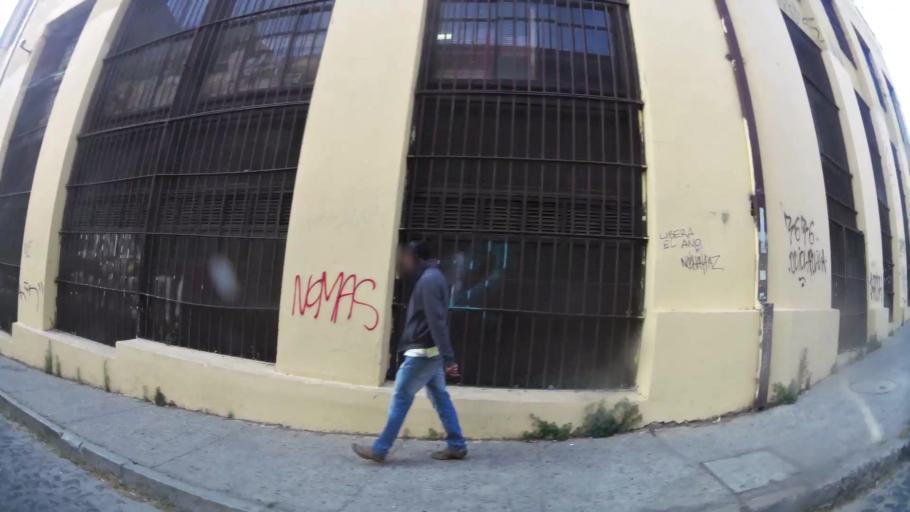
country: CL
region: Valparaiso
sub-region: Provincia de Valparaiso
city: Valparaiso
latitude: -33.0399
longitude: -71.6312
